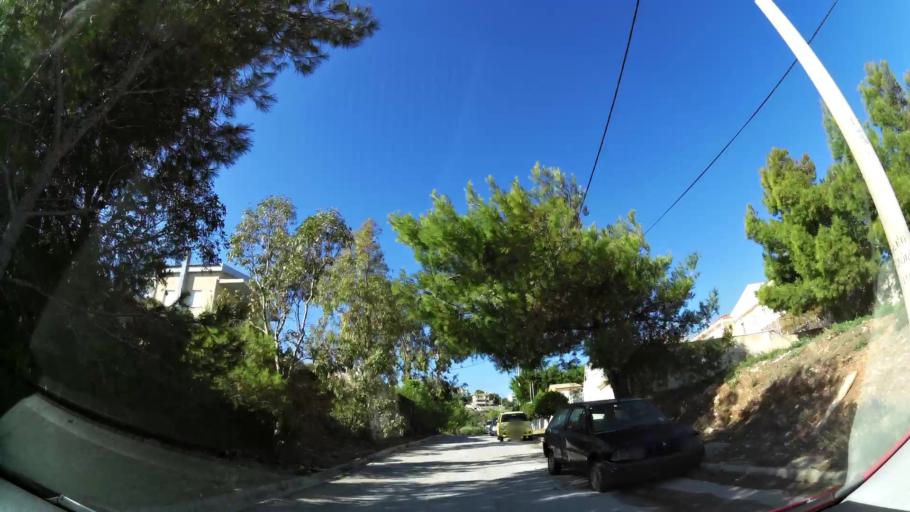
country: GR
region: Attica
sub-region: Nomarchia Anatolikis Attikis
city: Dhrafi
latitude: 38.0276
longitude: 23.9046
